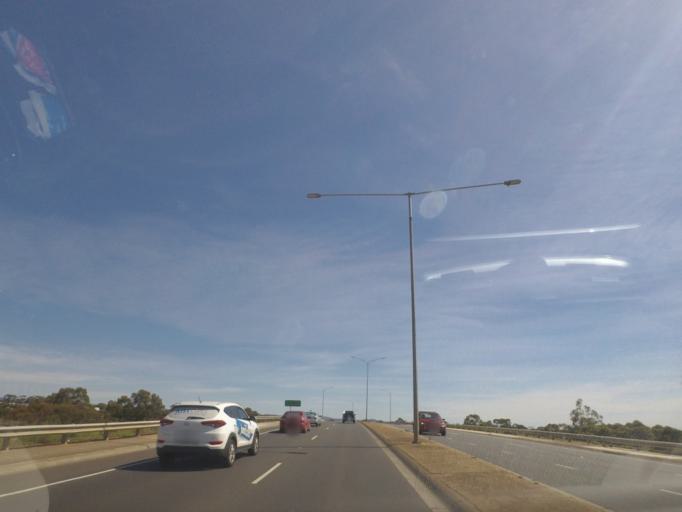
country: AU
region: Victoria
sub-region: Melton
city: Brookfield
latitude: -37.6916
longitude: 144.5667
